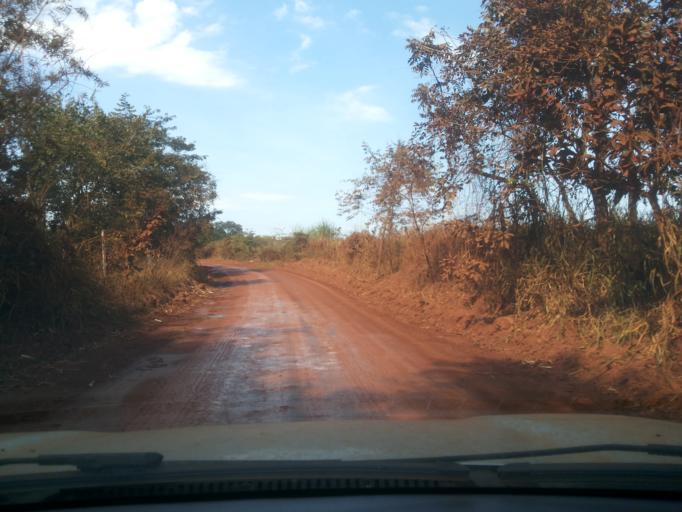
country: BR
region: Minas Gerais
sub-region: Ituiutaba
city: Ituiutaba
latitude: -19.0179
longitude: -49.3967
